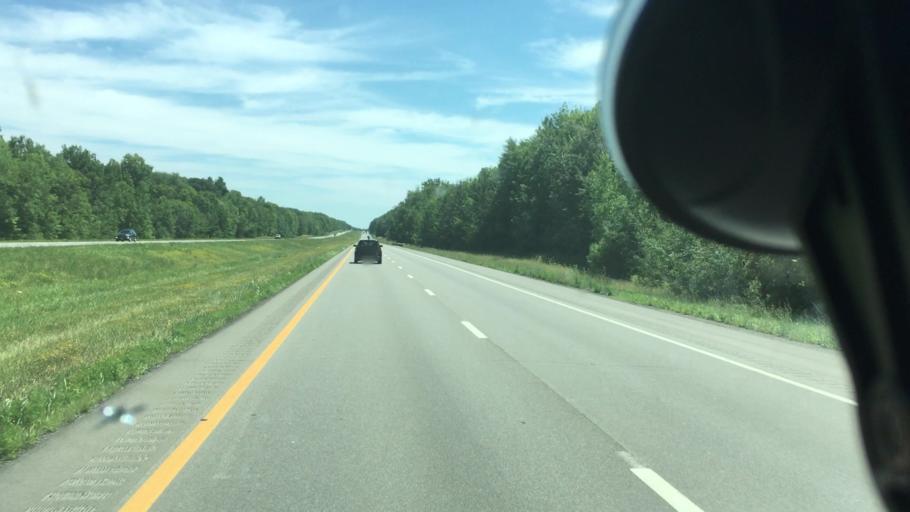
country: US
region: Ohio
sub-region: Mahoning County
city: Austintown
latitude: 41.0646
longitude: -80.7514
